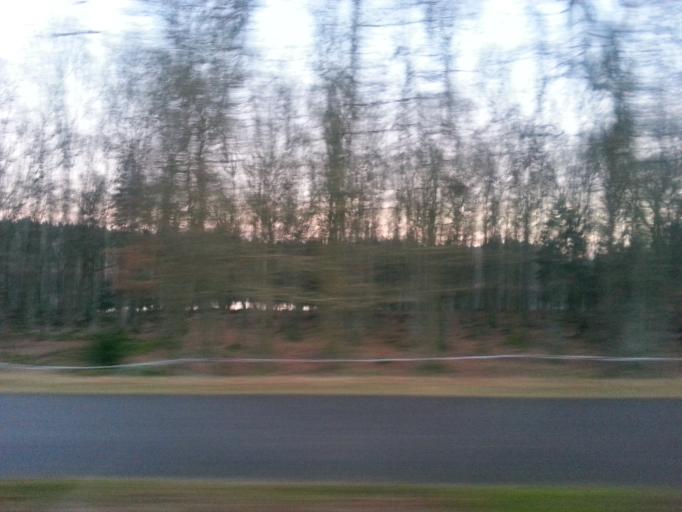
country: SE
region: Vaestra Goetaland
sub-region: Partille Kommun
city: Ojersjo
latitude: 57.6855
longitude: 12.1039
